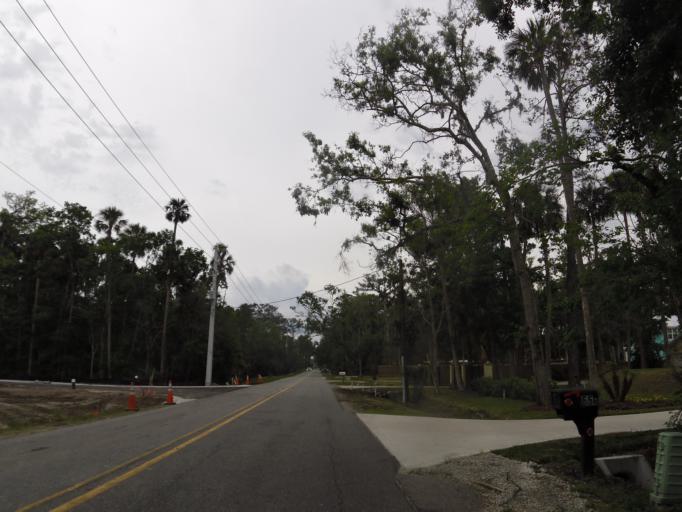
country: US
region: Florida
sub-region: Saint Johns County
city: Palm Valley
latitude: 30.1846
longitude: -81.4023
